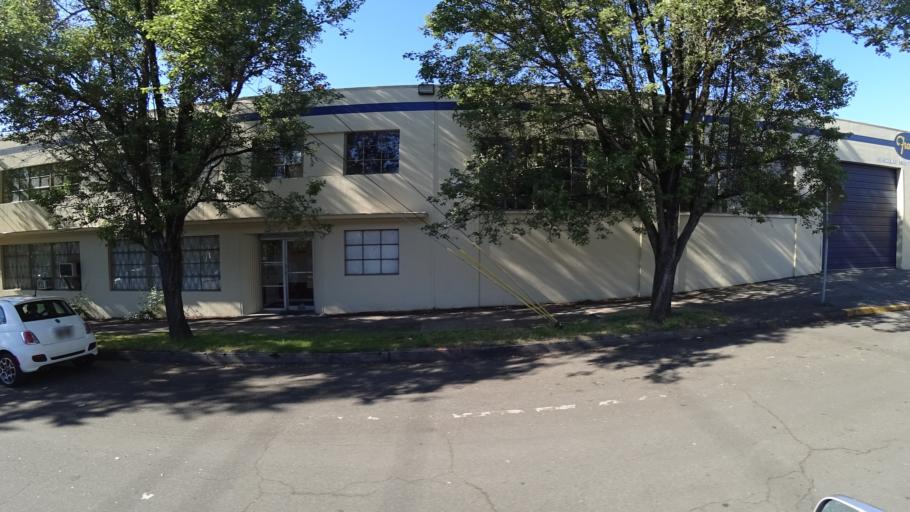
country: US
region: Oregon
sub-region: Multnomah County
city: Portland
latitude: 45.5249
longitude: -122.6557
